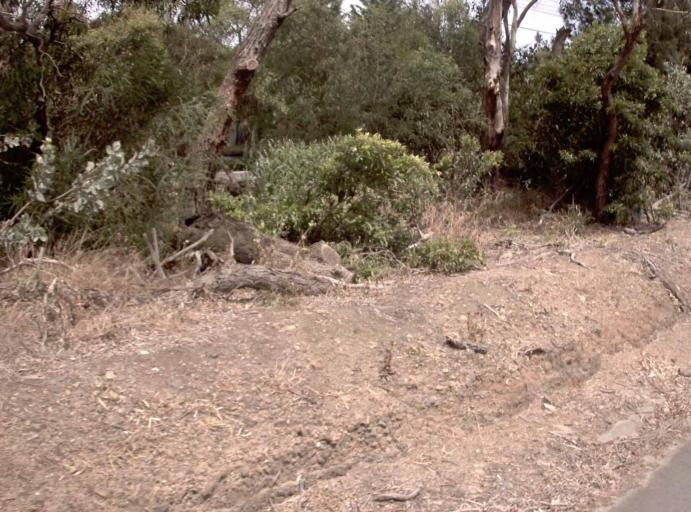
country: AU
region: Victoria
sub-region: Frankston
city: Frankston South
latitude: -38.1688
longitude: 145.1383
